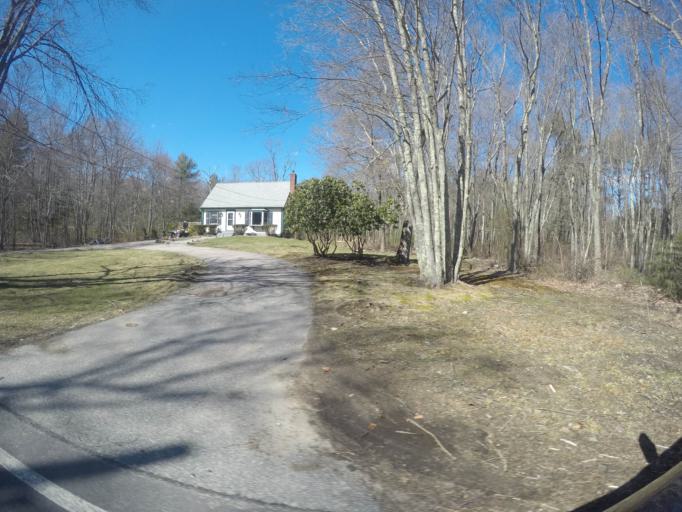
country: US
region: Massachusetts
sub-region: Bristol County
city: Easton
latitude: 42.0085
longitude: -71.1129
